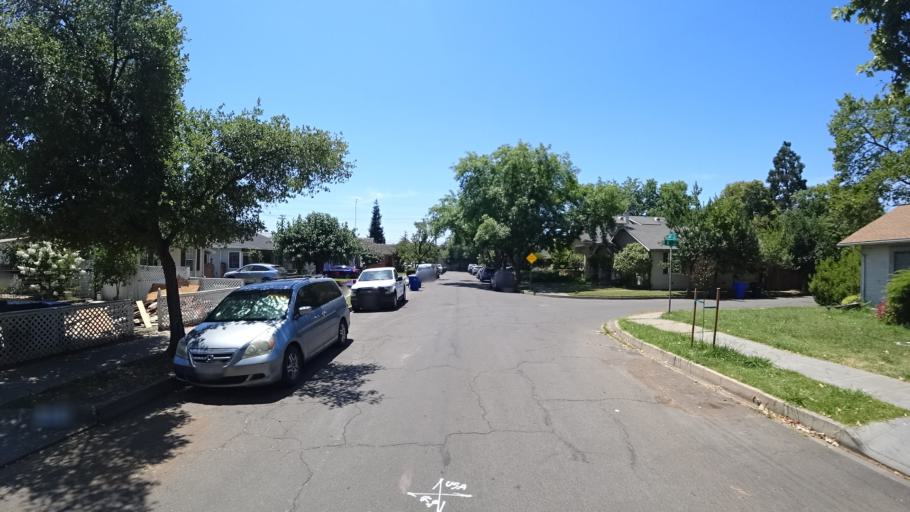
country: US
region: California
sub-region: Sacramento County
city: Sacramento
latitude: 38.5585
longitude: -121.4461
